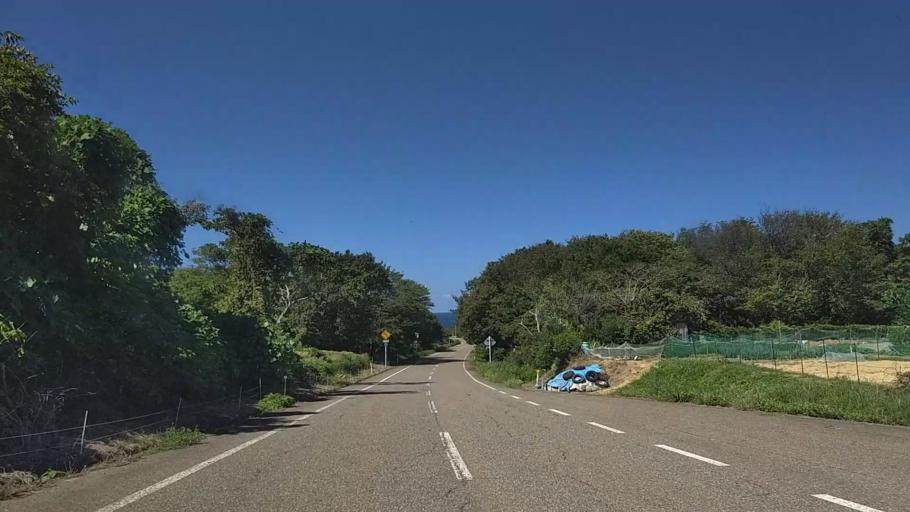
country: JP
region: Niigata
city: Joetsu
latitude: 37.1709
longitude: 138.1048
